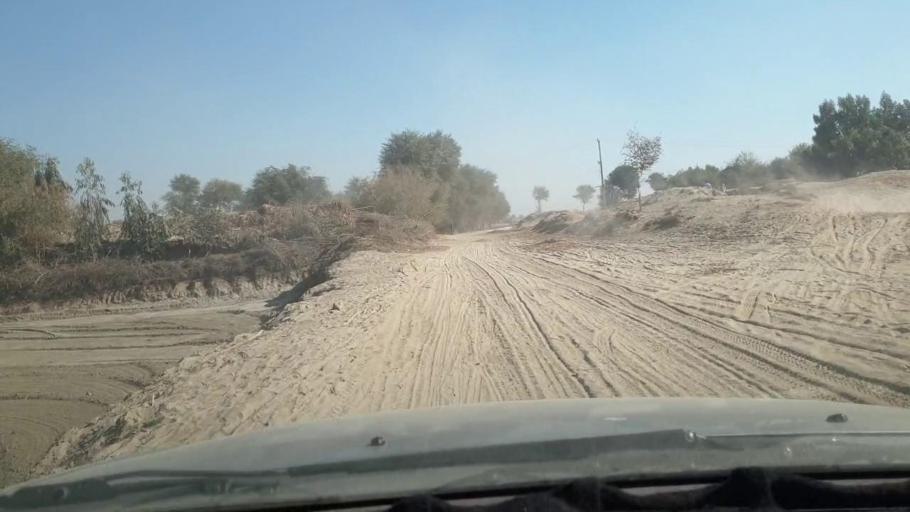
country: PK
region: Sindh
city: Ghotki
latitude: 28.0158
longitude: 69.2287
